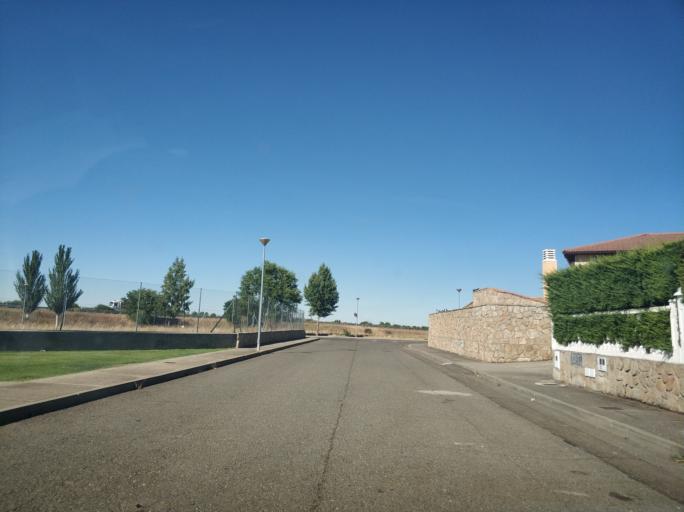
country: ES
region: Castille and Leon
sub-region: Provincia de Salamanca
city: Santa Marta de Tormes
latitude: 40.9432
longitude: -5.6195
